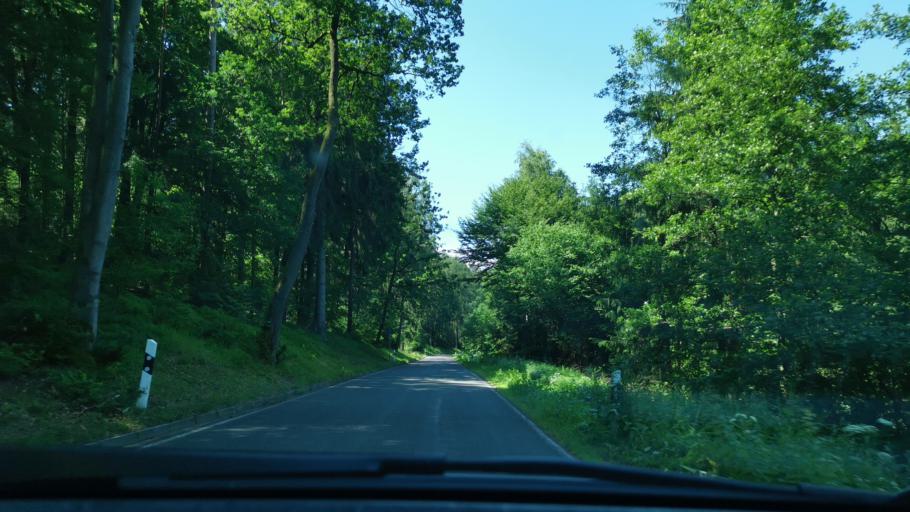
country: DE
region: Hesse
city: Hessisch Lichtenau
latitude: 51.1597
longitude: 9.7526
